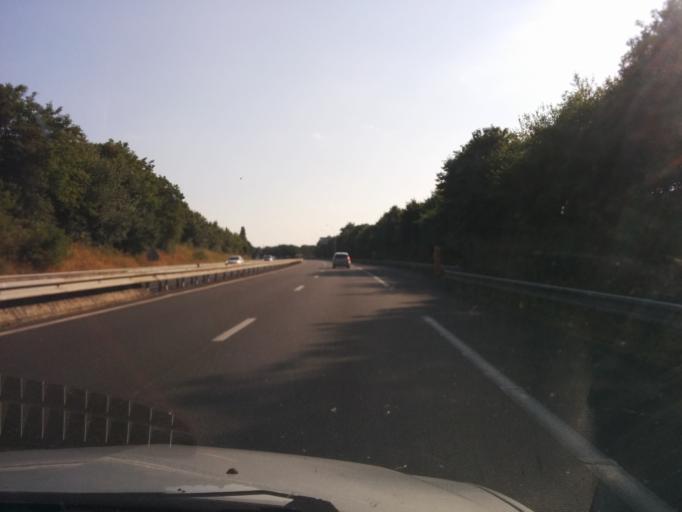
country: FR
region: Pays de la Loire
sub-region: Departement de la Loire-Atlantique
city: Carquefou
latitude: 47.2885
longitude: -1.5042
